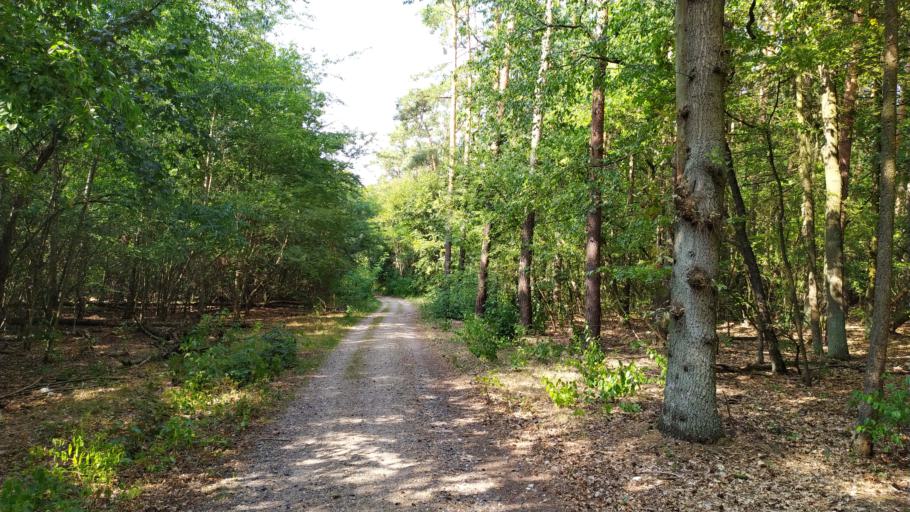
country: DE
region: Berlin
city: Grunau
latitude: 52.4140
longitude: 13.6069
